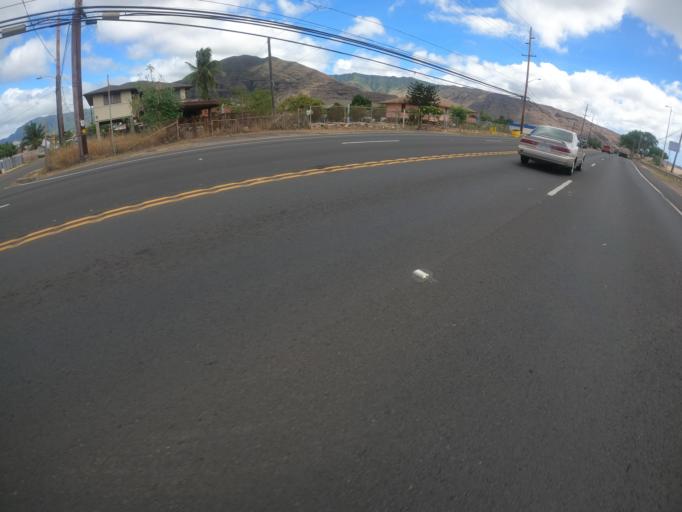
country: US
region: Hawaii
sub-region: Honolulu County
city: Nanakuli
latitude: 21.3929
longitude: -158.1578
